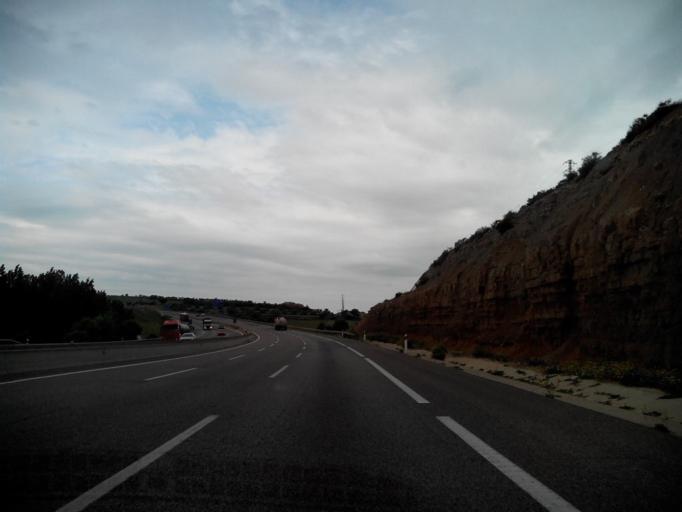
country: ES
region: Catalonia
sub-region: Provincia de Lleida
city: Cervera
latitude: 41.6817
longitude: 1.2382
